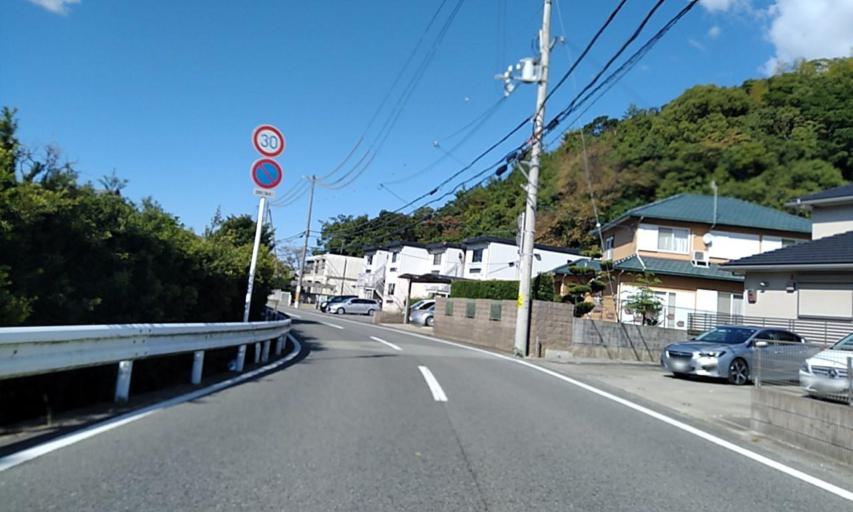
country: JP
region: Wakayama
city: Wakayama-shi
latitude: 34.1981
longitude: 135.1899
